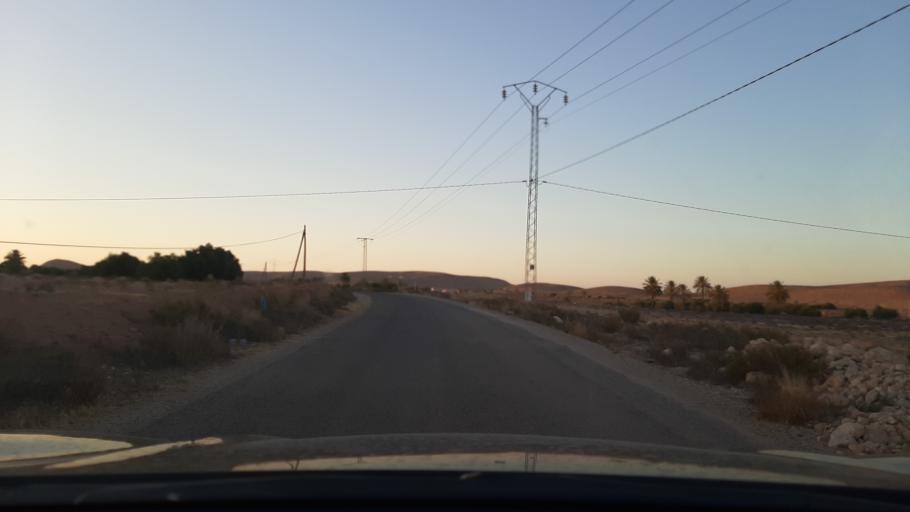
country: TN
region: Qabis
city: Matmata
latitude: 33.5553
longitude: 10.1855
